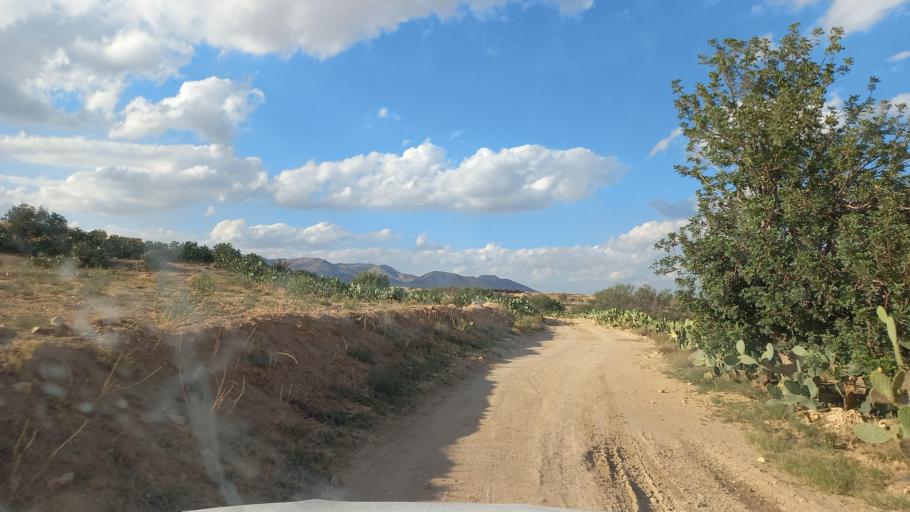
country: TN
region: Al Qasrayn
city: Sbiba
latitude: 35.3831
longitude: 9.0724
